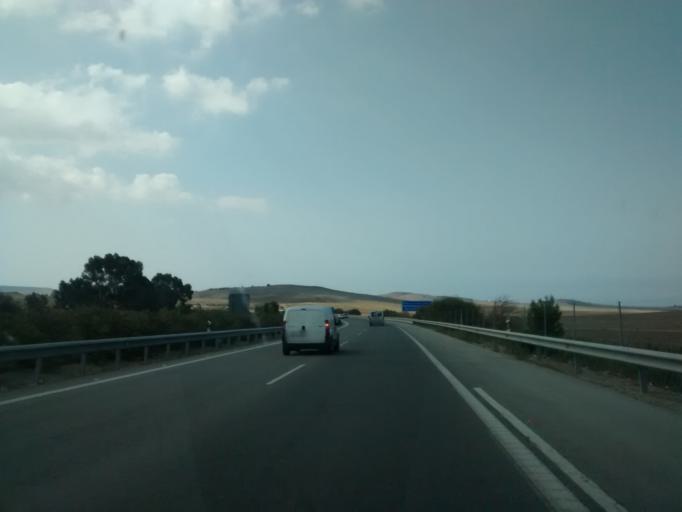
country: ES
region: Andalusia
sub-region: Provincia de Cadiz
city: Conil de la Frontera
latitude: 36.2667
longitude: -6.0290
